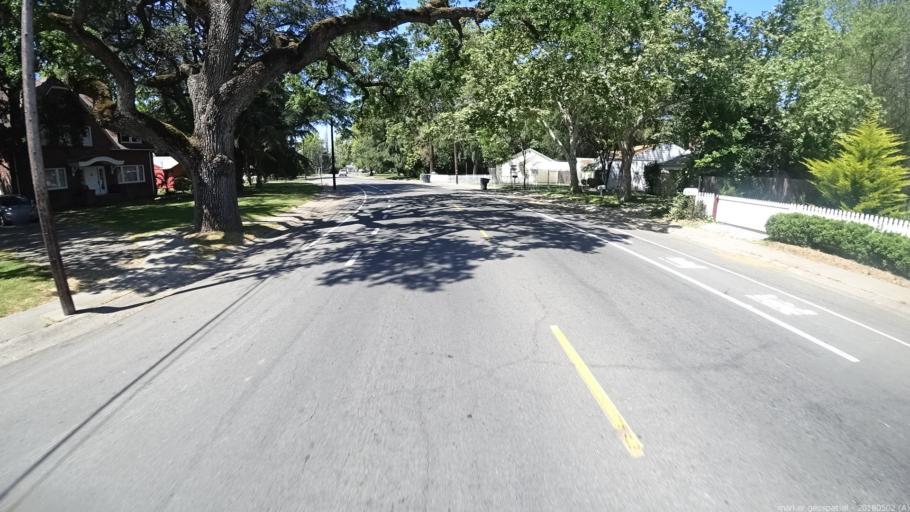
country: US
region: California
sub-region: Sacramento County
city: Rio Linda
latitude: 38.6261
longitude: -121.4417
